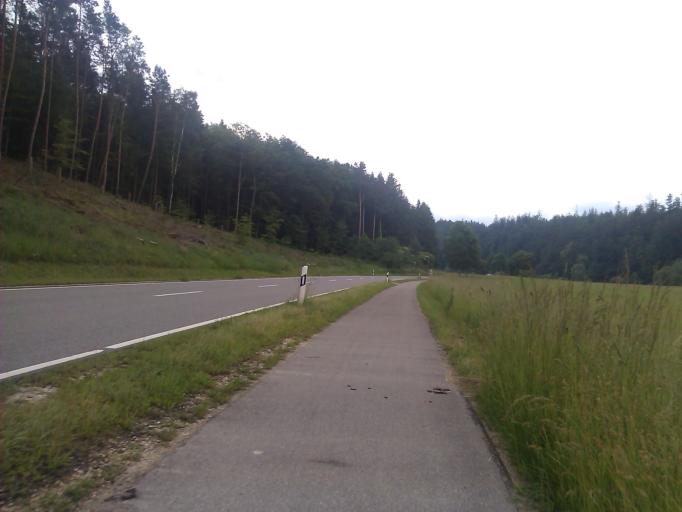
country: DE
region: Baden-Wuerttemberg
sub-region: Regierungsbezirk Stuttgart
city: Abtsgmund
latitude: 48.9059
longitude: 9.9747
